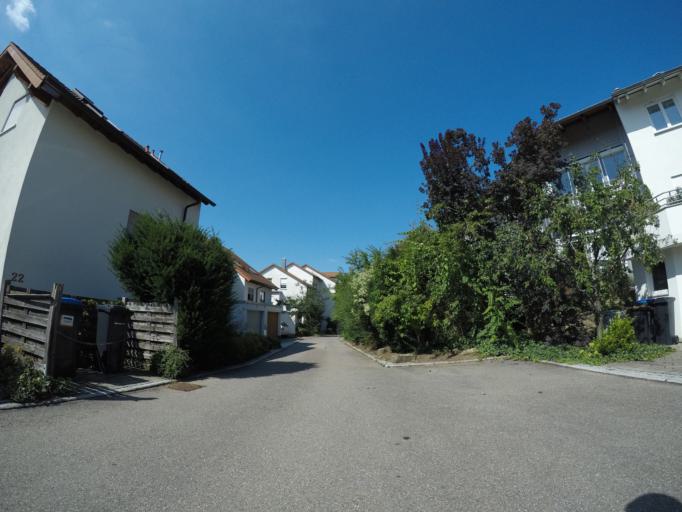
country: DE
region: Baden-Wuerttemberg
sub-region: Tuebingen Region
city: Eningen unter Achalm
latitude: 48.4823
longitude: 9.2578
